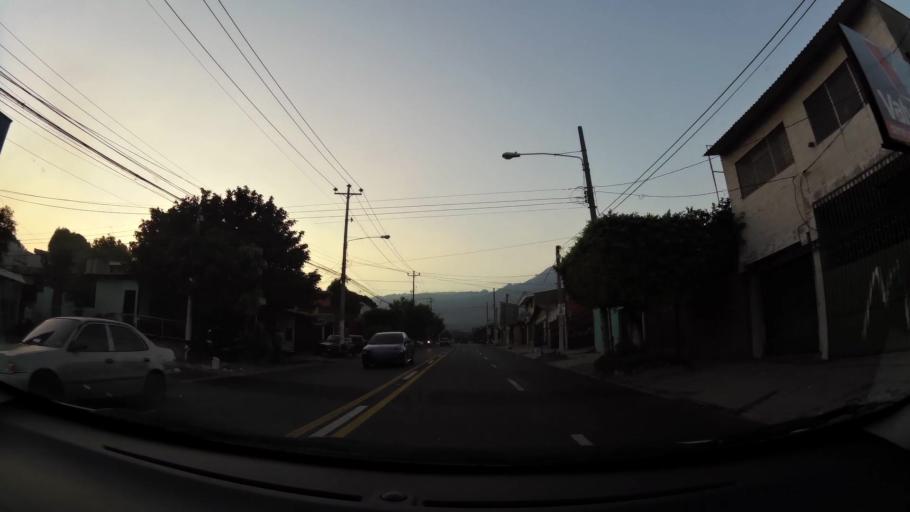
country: SV
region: San Salvador
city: Mejicanos
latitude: 13.7171
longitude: -89.2199
